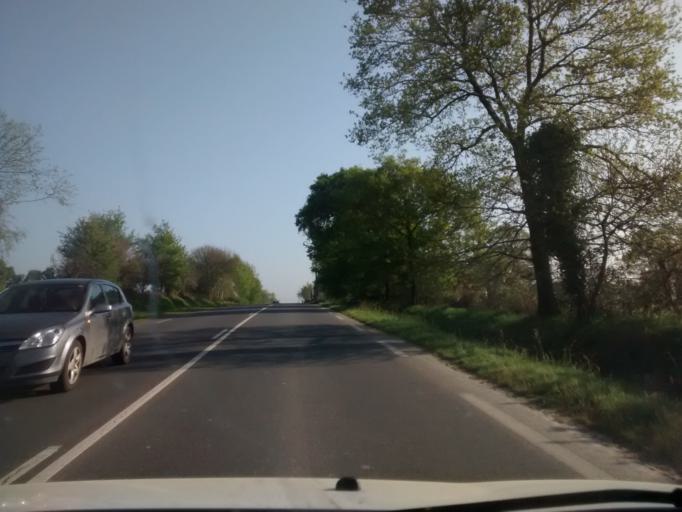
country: FR
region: Brittany
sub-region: Departement d'Ille-et-Vilaine
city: Saint-Aubin-du-Cormier
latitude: 48.2709
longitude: -1.3911
